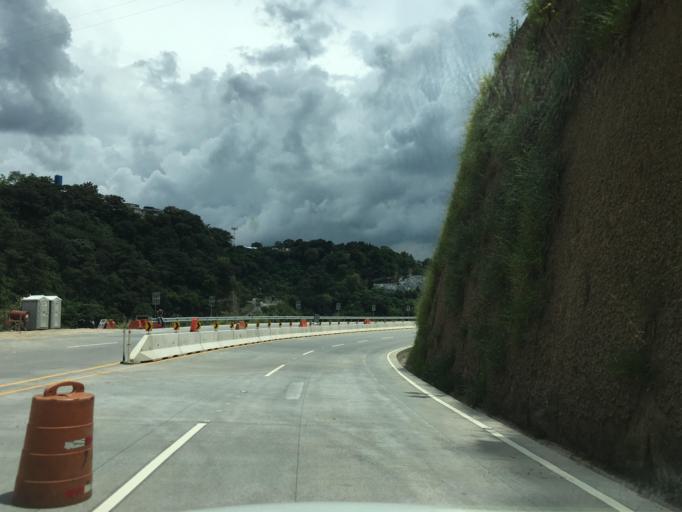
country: GT
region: Guatemala
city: Santa Catarina Pinula
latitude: 14.5505
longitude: -90.5320
